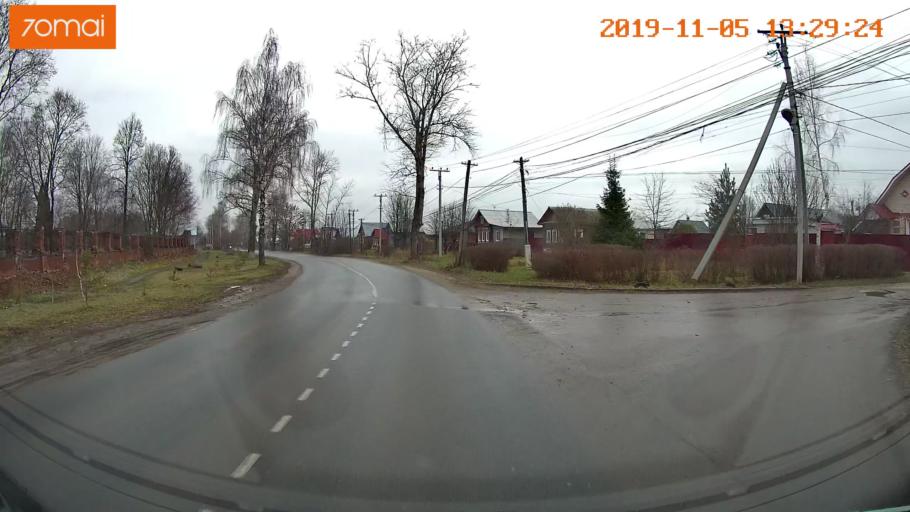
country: RU
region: Ivanovo
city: Shuya
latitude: 56.8603
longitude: 41.3975
